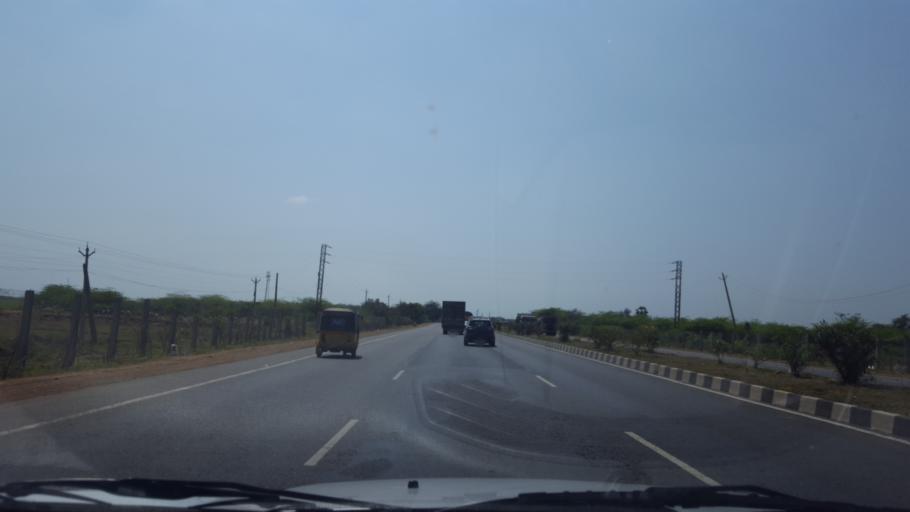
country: IN
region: Andhra Pradesh
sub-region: Prakasam
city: Ongole
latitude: 15.4440
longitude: 80.0474
